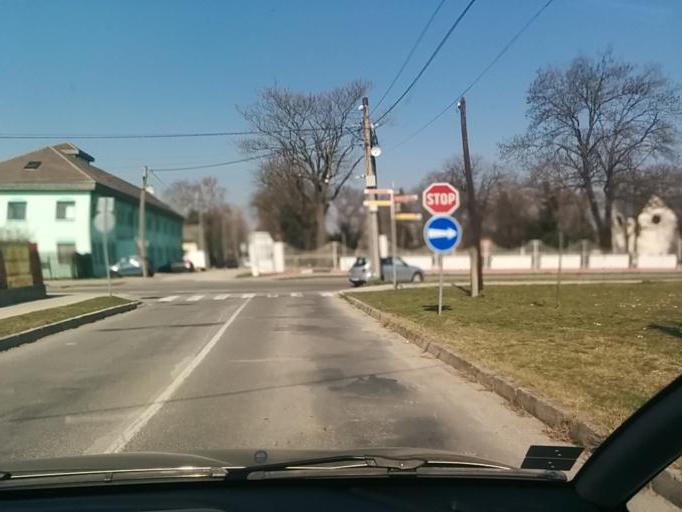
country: SK
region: Trnavsky
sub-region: Okres Galanta
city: Galanta
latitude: 48.1882
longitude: 17.7221
